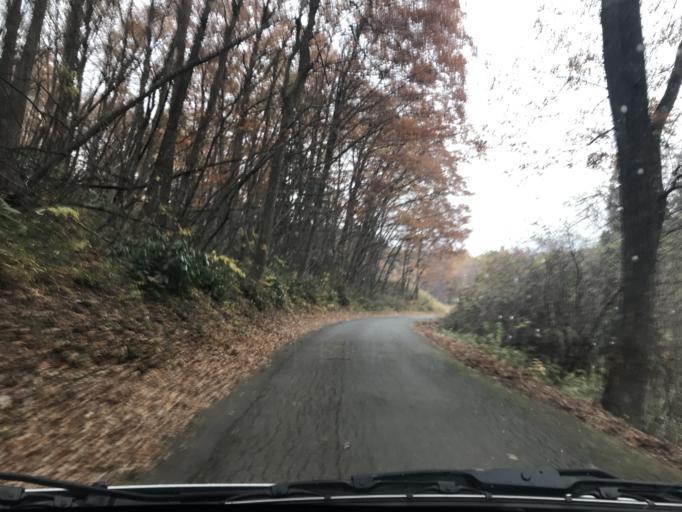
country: JP
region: Iwate
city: Ichinoseki
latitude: 38.9789
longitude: 141.0014
